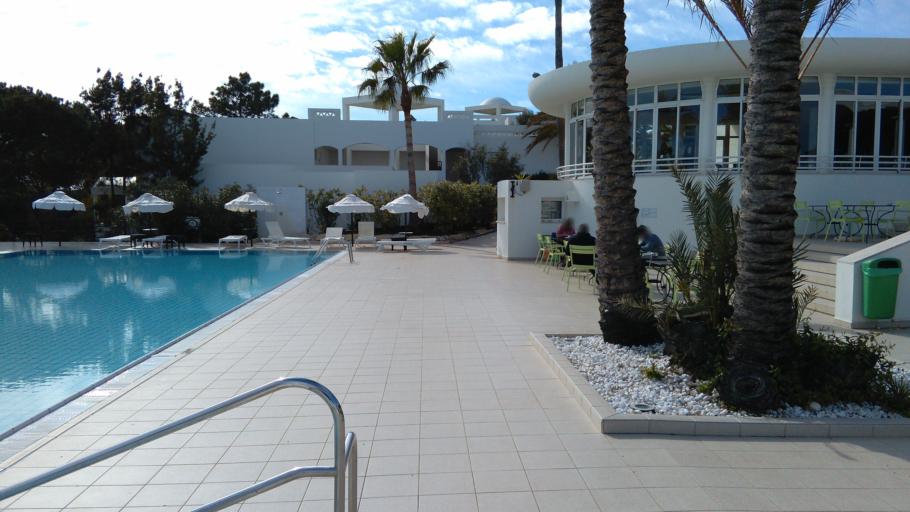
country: PT
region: Faro
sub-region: Albufeira
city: Albufeira
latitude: 37.0755
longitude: -8.2961
